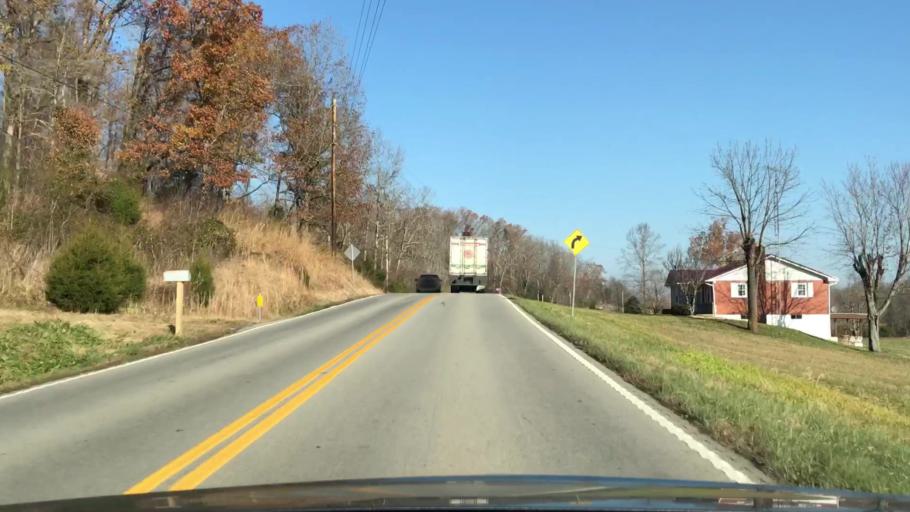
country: US
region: Kentucky
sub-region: Grayson County
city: Leitchfield
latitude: 37.4484
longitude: -86.2905
